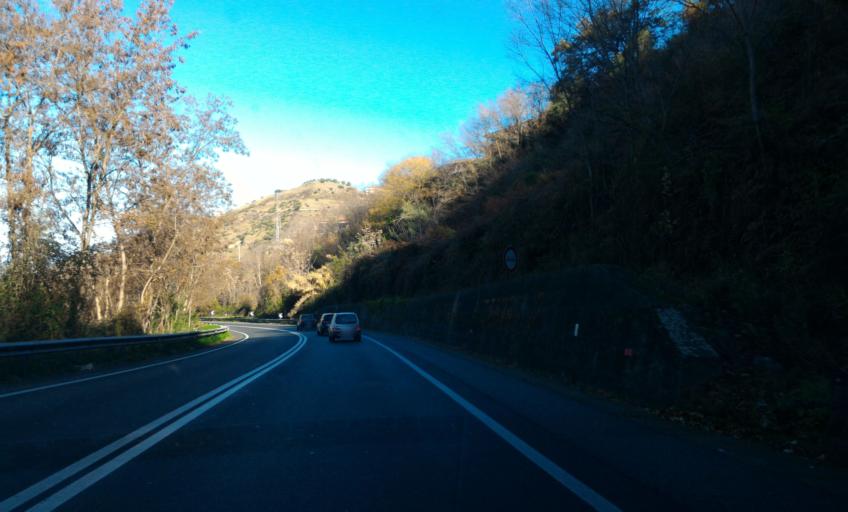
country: IT
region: Calabria
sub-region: Provincia di Cosenza
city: Cosenza
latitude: 39.3001
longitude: 16.2651
